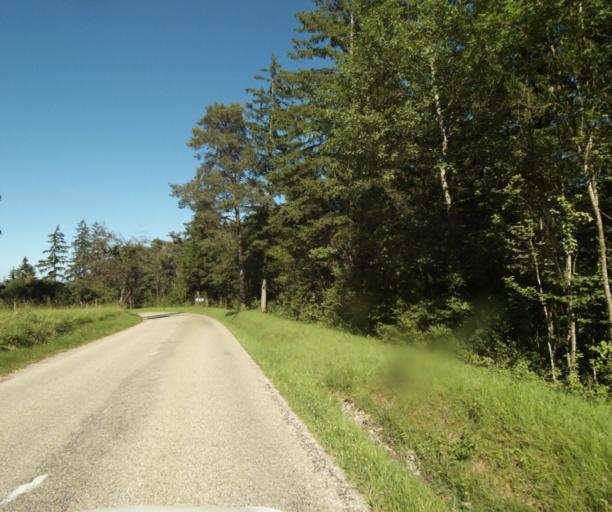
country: FR
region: Rhone-Alpes
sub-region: Departement de la Haute-Savoie
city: Sciez
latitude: 46.3168
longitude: 6.3852
